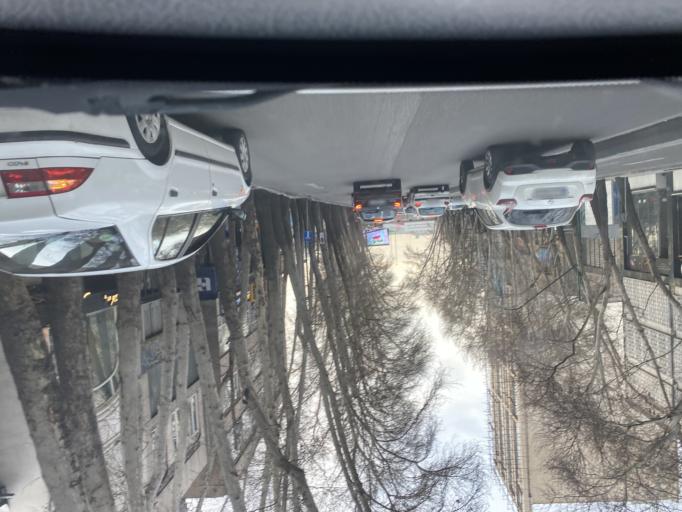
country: IR
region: Tehran
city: Tajrish
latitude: 35.7927
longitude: 51.4166
